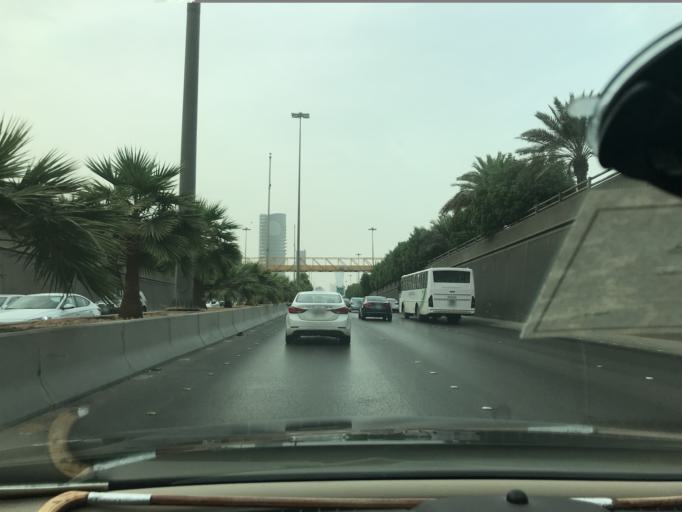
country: SA
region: Ar Riyad
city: Riyadh
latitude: 24.7132
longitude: 46.6712
